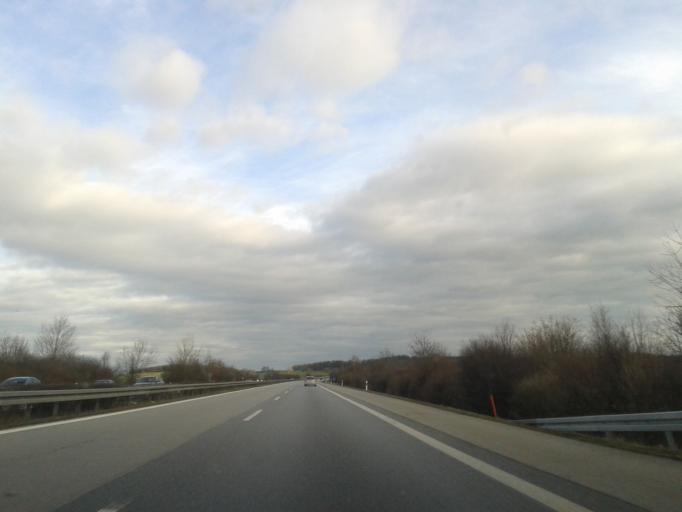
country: DE
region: Saxony
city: Kubschutz
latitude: 51.2019
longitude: 14.4809
